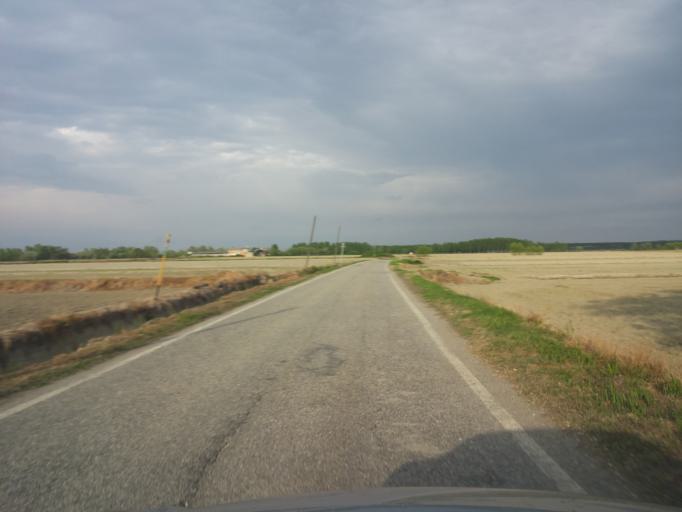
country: IT
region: Piedmont
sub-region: Provincia di Vercelli
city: Motta De Conti
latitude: 45.1855
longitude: 8.5183
